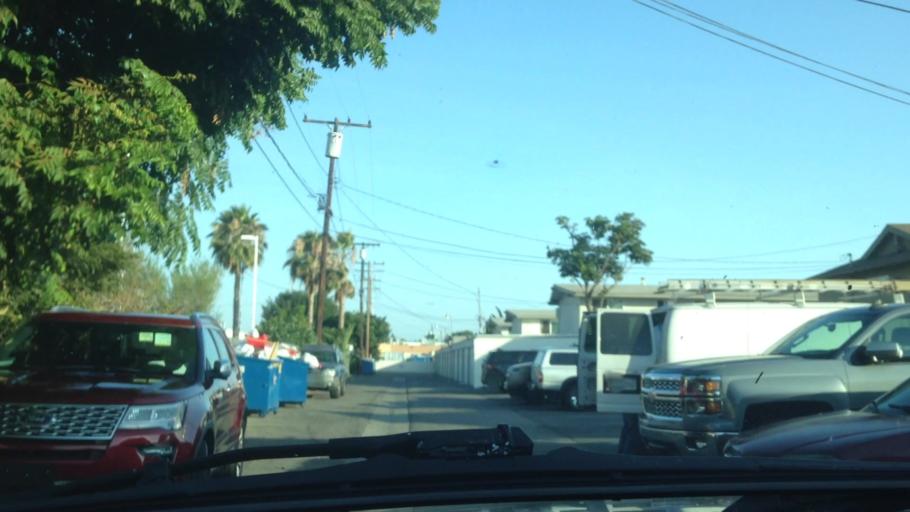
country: US
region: California
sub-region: Orange County
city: Anaheim
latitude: 33.8210
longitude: -117.9104
